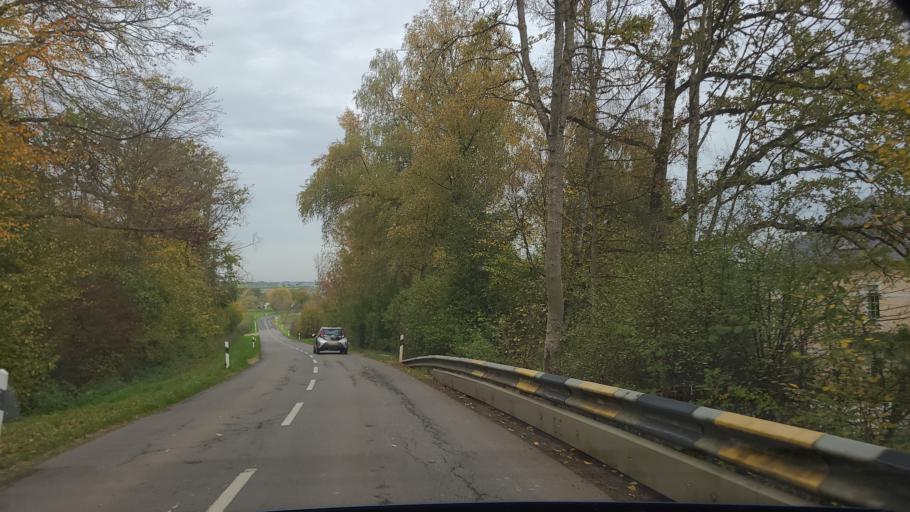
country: LU
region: Luxembourg
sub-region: Canton de Capellen
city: Dippach
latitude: 49.6092
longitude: 5.9925
